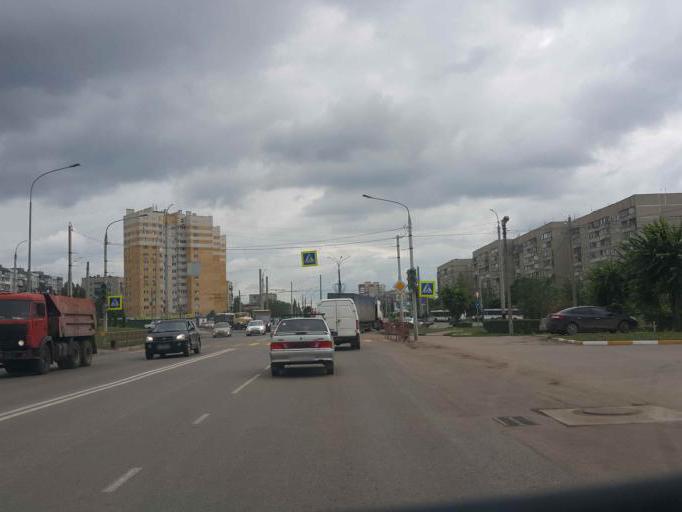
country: RU
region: Tambov
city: Tambov
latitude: 52.7619
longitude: 41.4007
